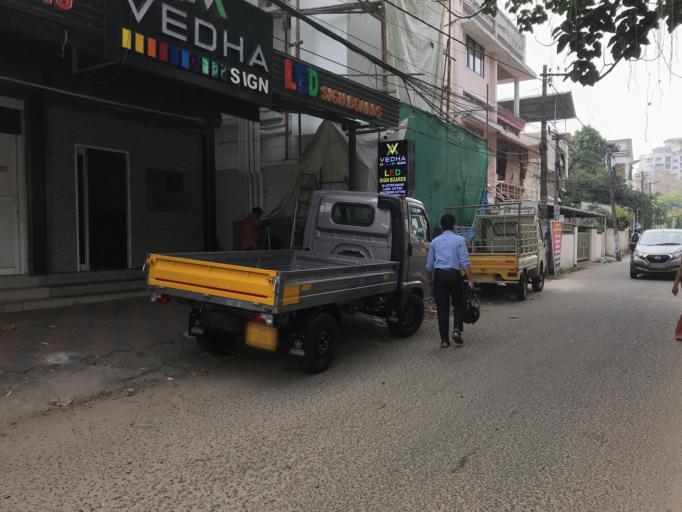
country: IN
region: Kerala
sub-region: Ernakulam
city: Elur
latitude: 10.0006
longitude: 76.2929
